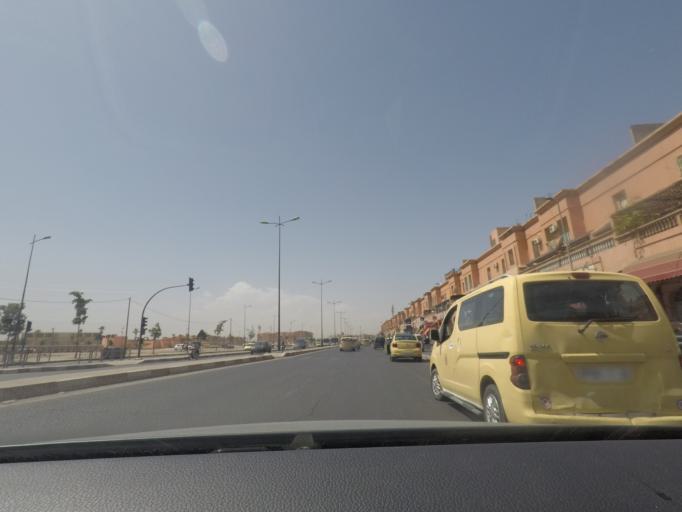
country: MA
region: Marrakech-Tensift-Al Haouz
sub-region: Marrakech
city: Marrakesh
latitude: 31.5940
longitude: -8.0297
